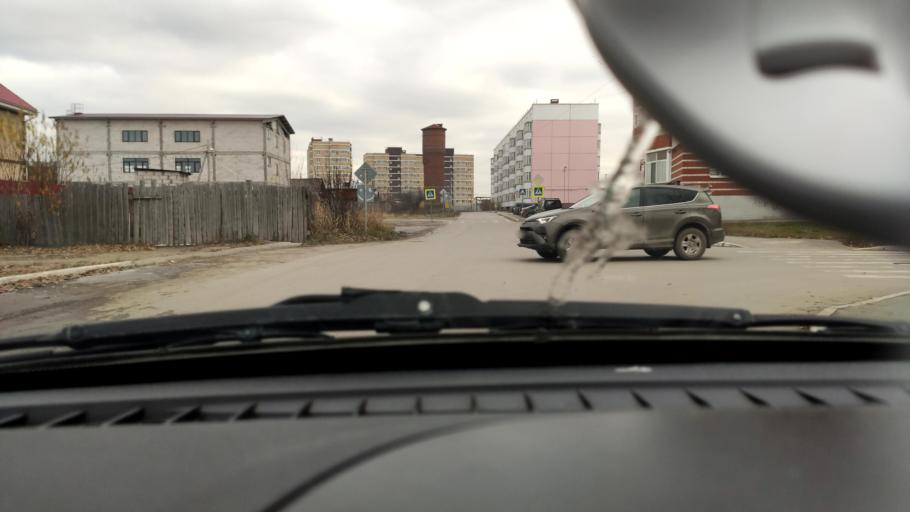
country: RU
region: Perm
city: Kondratovo
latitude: 57.9794
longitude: 56.1029
